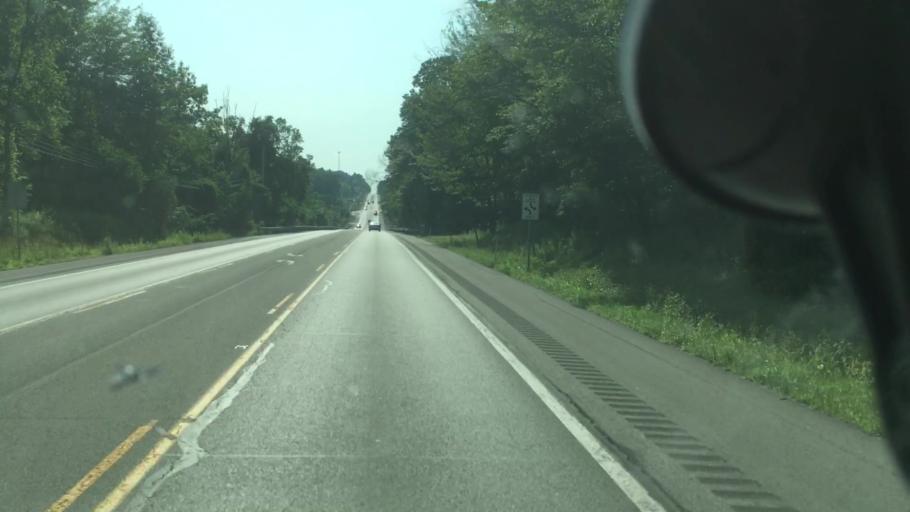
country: US
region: Pennsylvania
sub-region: Lawrence County
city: New Castle
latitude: 40.9750
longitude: -80.2740
